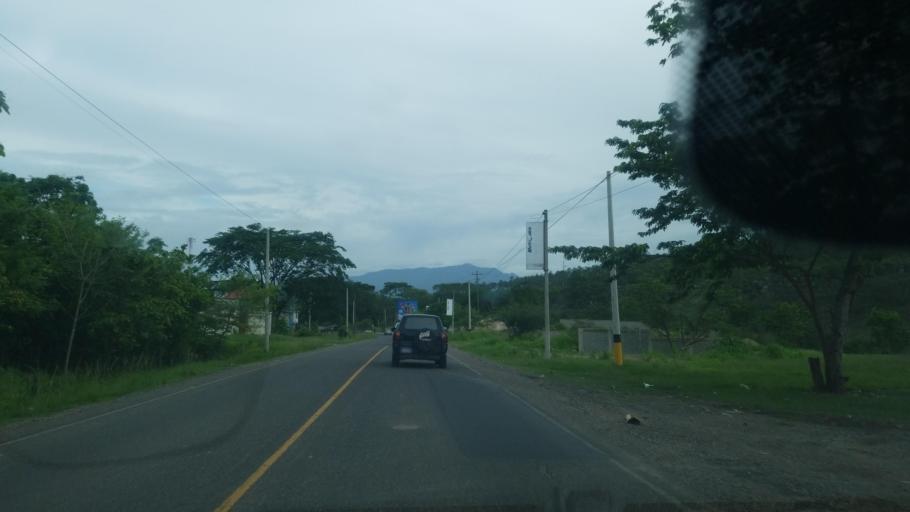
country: HN
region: Santa Barbara
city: Santa Barbara
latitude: 14.9098
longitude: -88.2524
